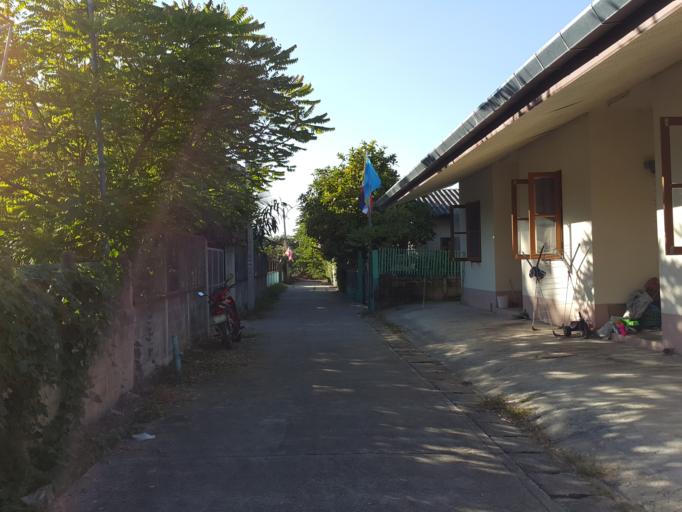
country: TH
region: Chiang Mai
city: San Kamphaeng
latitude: 18.7766
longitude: 99.0860
